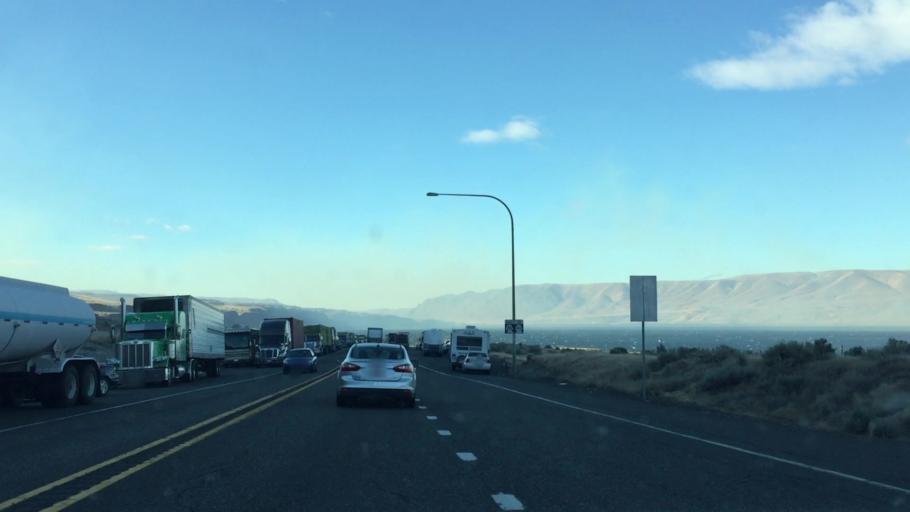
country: US
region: Washington
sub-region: Grant County
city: Mattawa
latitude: 46.9420
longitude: -119.9617
